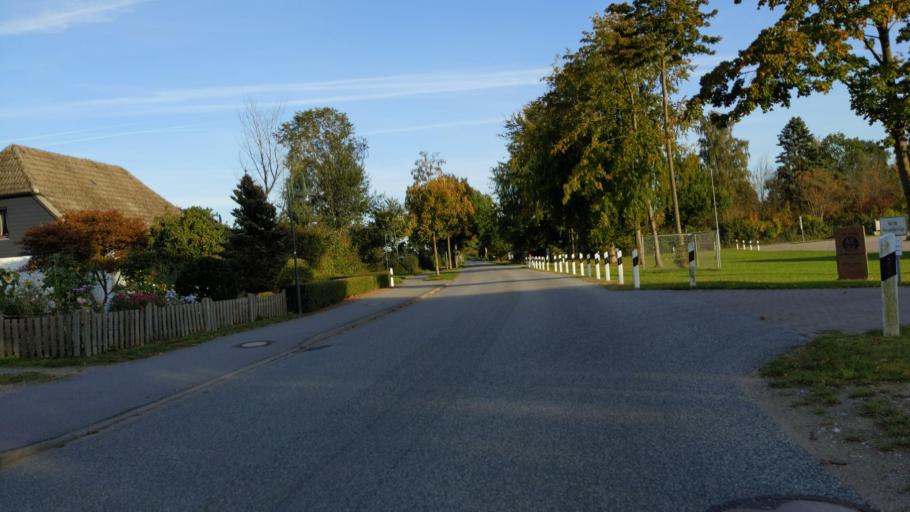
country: DE
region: Schleswig-Holstein
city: Susel
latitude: 54.0808
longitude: 10.7031
